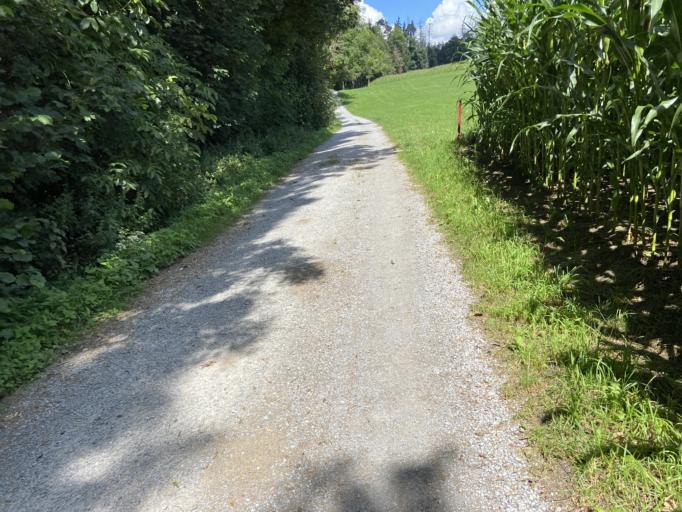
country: CH
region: Zurich
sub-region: Bezirk Meilen
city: Oetwil am See
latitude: 47.2578
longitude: 8.7164
